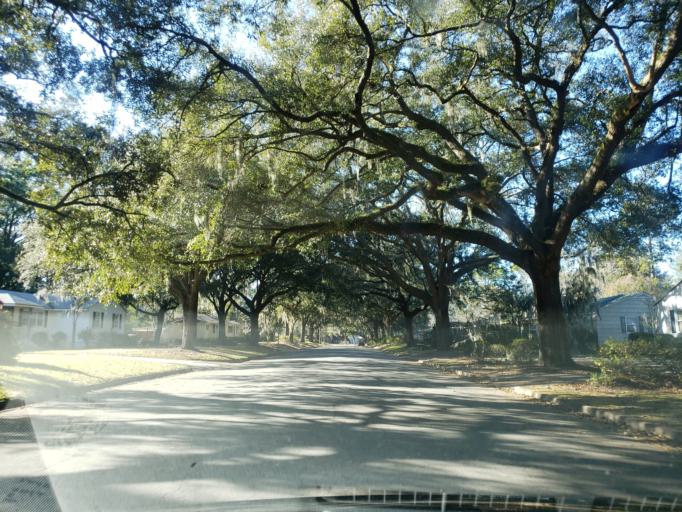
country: US
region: Georgia
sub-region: Chatham County
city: Thunderbolt
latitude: 32.0249
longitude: -81.1001
